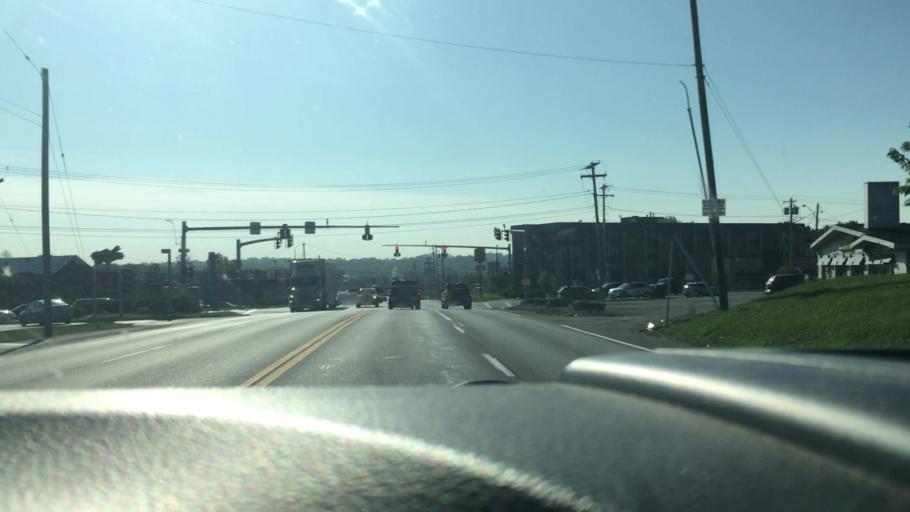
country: US
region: New York
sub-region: Onondaga County
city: Galeville
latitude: 43.0929
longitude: -76.1723
